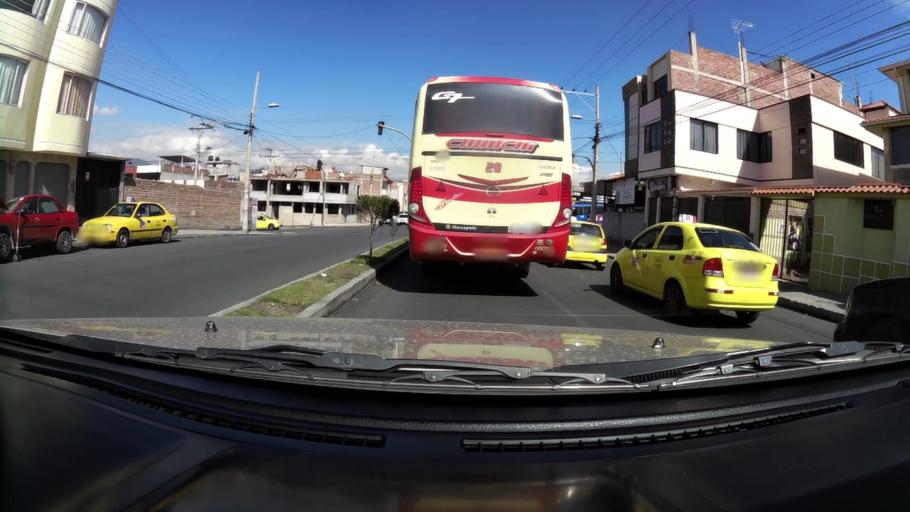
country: EC
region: Chimborazo
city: Riobamba
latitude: -1.6611
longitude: -78.6692
